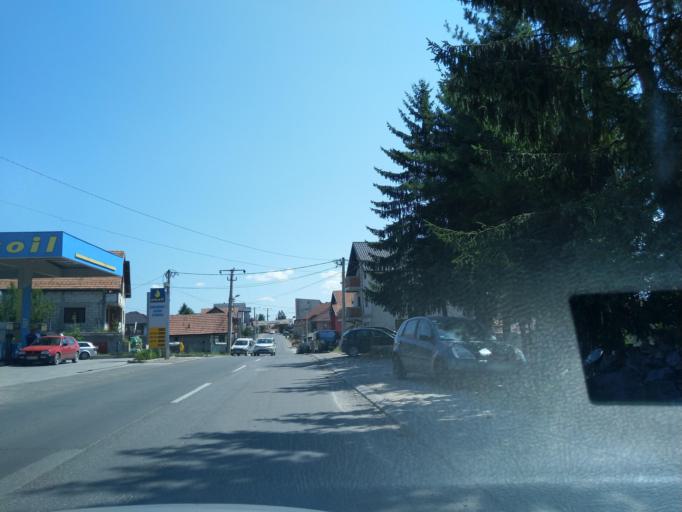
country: RS
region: Central Serbia
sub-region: Zlatiborski Okrug
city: Sjenica
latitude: 43.2766
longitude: 19.9907
